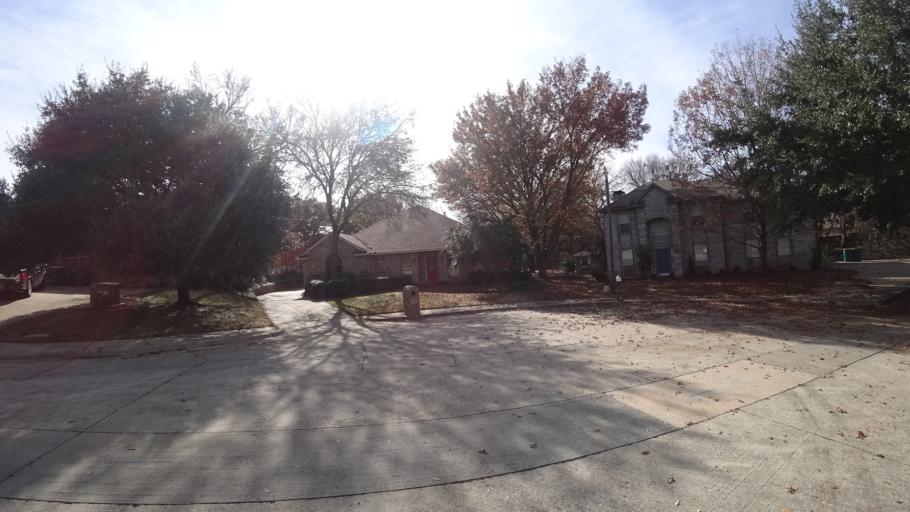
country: US
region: Texas
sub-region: Denton County
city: Highland Village
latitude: 33.0786
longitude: -97.0430
